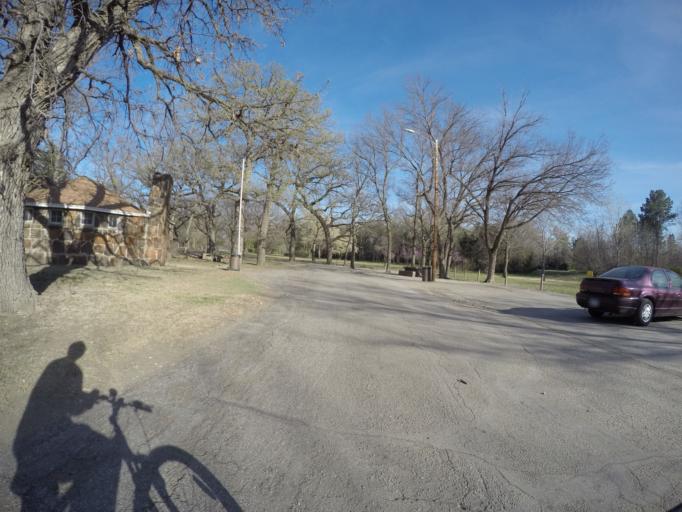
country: US
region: Kansas
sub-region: Saline County
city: Salina
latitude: 38.8668
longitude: -97.6156
